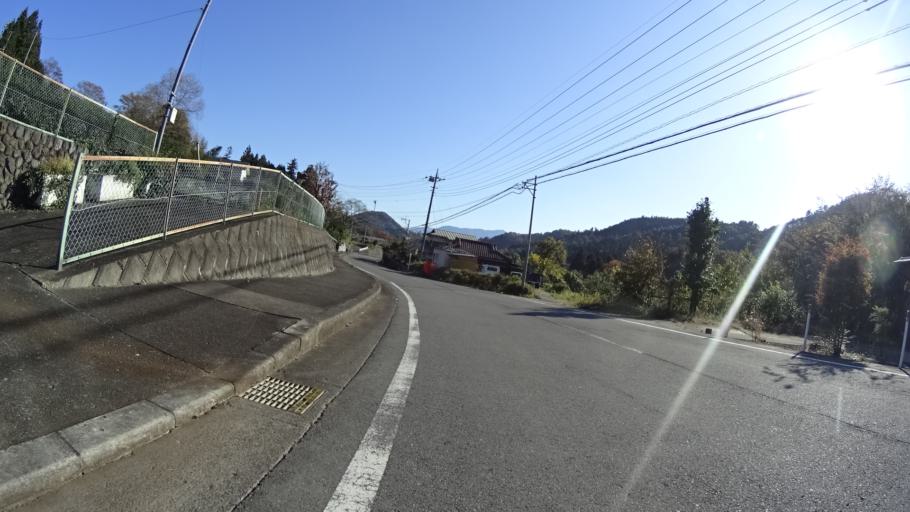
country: JP
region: Yamanashi
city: Uenohara
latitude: 35.6518
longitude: 139.1208
